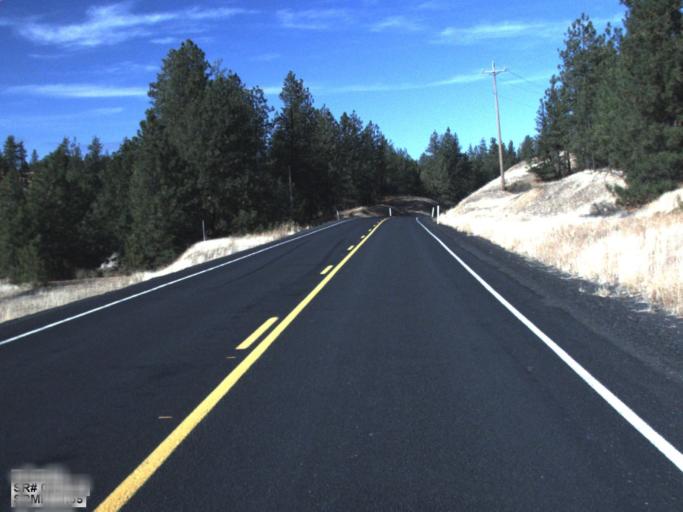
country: US
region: Washington
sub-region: Lincoln County
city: Davenport
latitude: 47.8145
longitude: -118.1819
